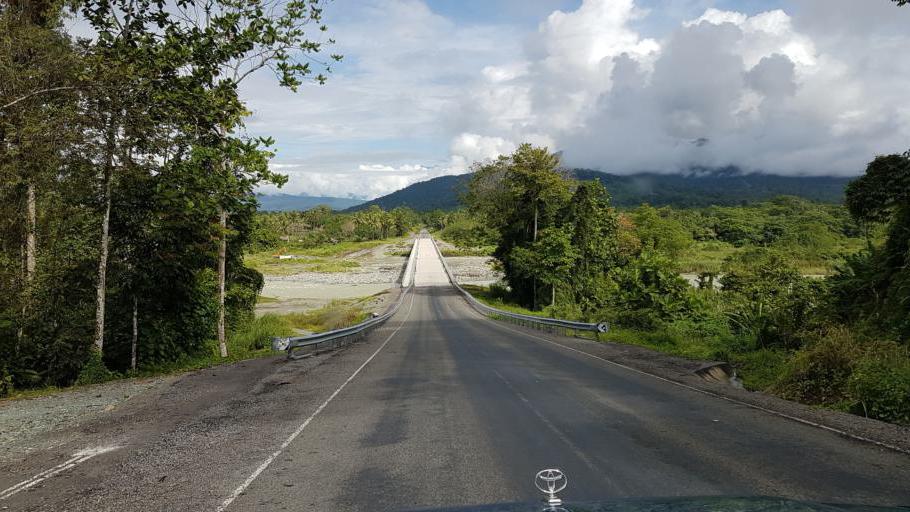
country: PG
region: Northern Province
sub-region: Sohe
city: Kokoda
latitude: -8.9053
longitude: 147.9836
